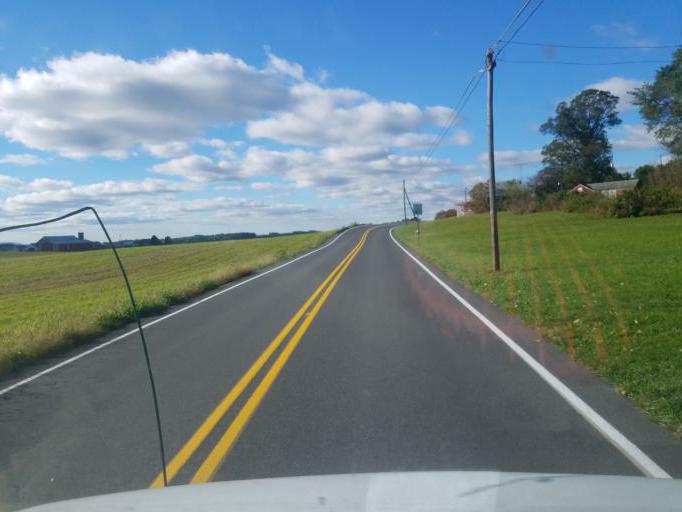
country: US
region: Pennsylvania
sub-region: Franklin County
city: Guilford Siding
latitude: 39.8344
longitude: -77.6286
